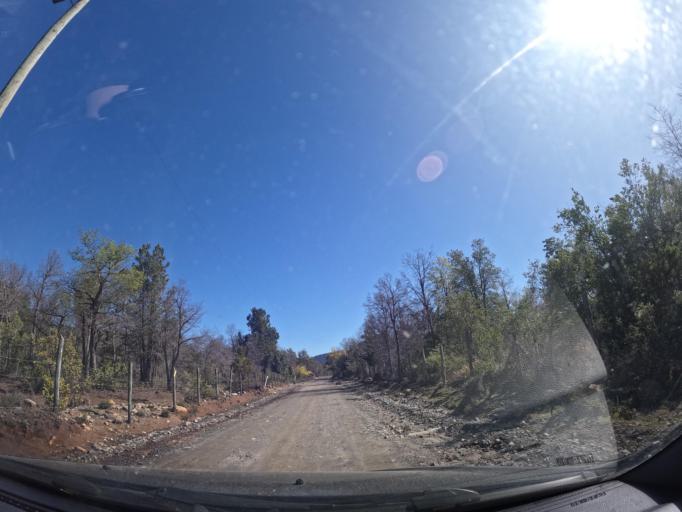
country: CL
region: Maule
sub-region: Provincia de Linares
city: Longavi
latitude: -36.2434
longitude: -71.3471
